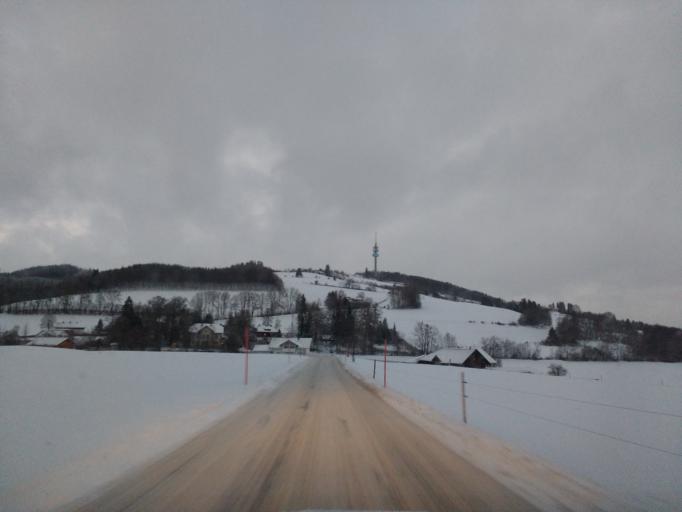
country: DE
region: Bavaria
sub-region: Swabia
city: Buchenberg
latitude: 47.7169
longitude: 10.2172
